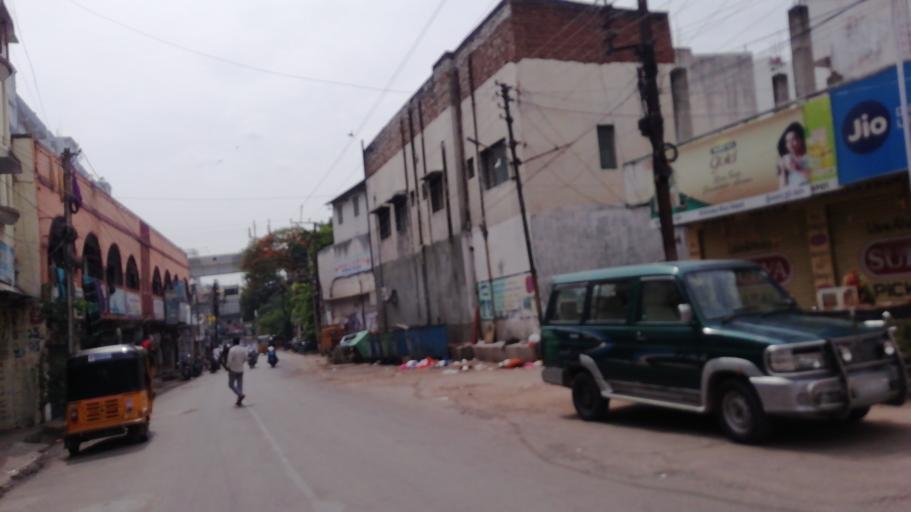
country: IN
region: Telangana
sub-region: Hyderabad
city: Malkajgiri
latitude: 17.4151
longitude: 78.4997
